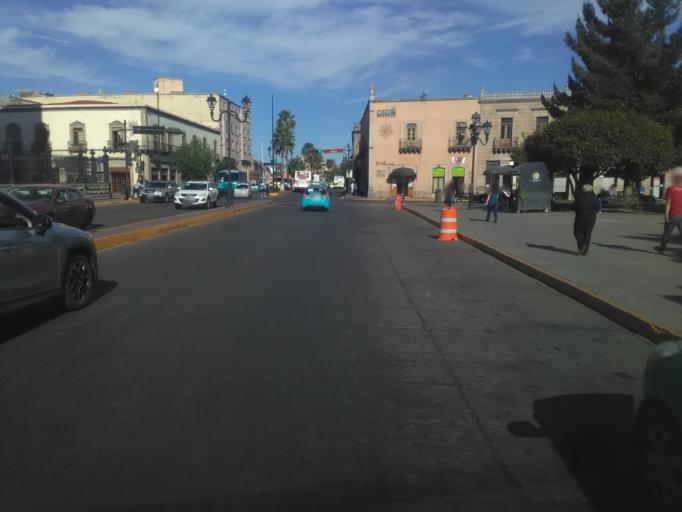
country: MX
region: Durango
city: Victoria de Durango
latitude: 24.0245
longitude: -104.6704
